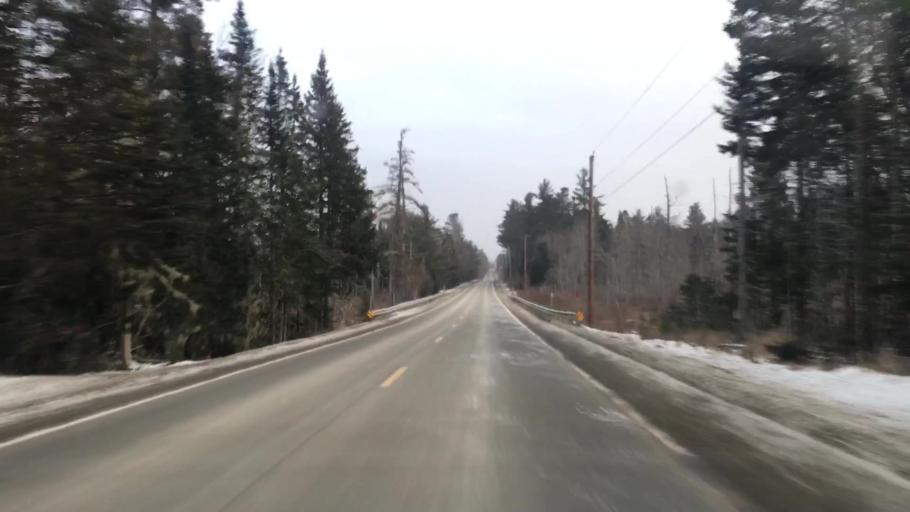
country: US
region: Maine
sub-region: Hancock County
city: Ellsworth
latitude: 44.6712
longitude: -68.3543
